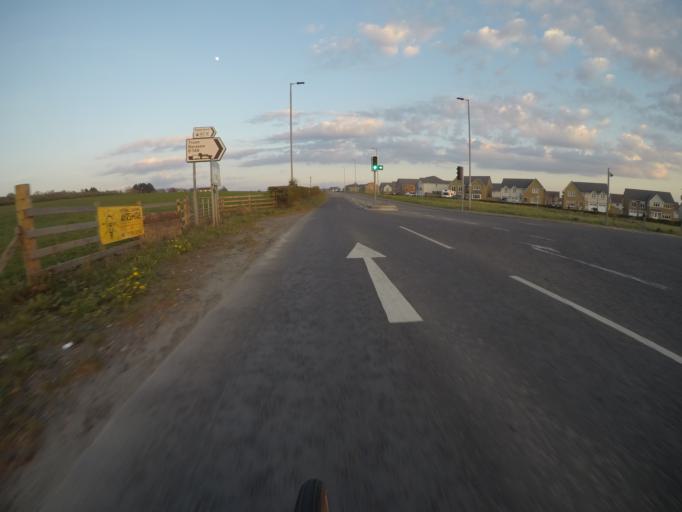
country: GB
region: Scotland
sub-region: South Ayrshire
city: Troon
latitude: 55.5648
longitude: -4.6372
